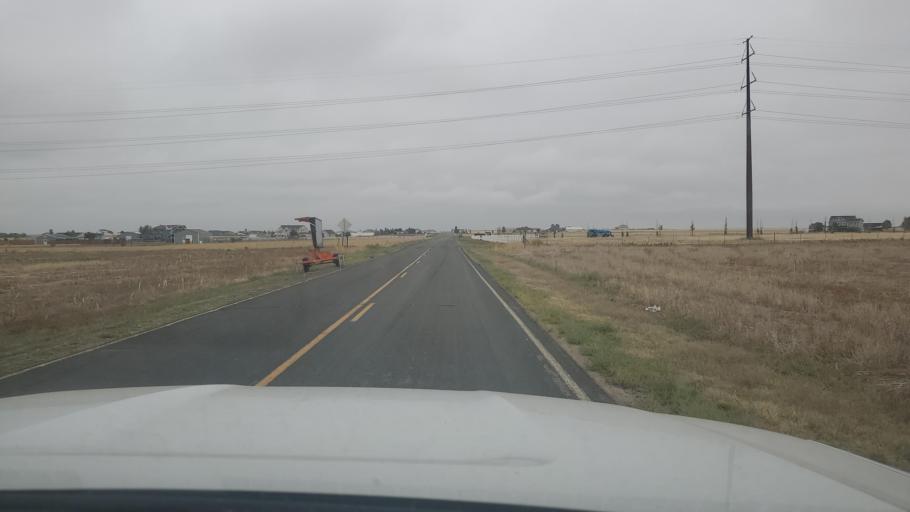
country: US
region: Colorado
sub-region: Weld County
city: Lochbuie
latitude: 39.9417
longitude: -104.6027
